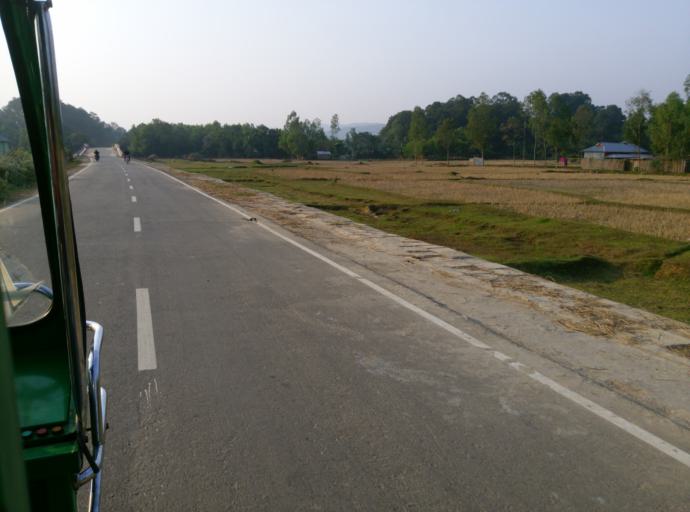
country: BD
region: Dhaka
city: Netrakona
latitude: 25.1737
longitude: 90.6554
